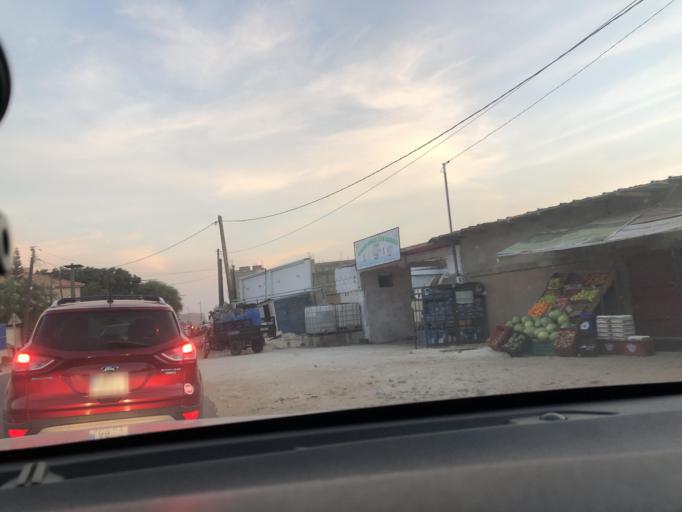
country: SN
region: Dakar
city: Mermoz Boabab
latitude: 14.7371
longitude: -17.5132
